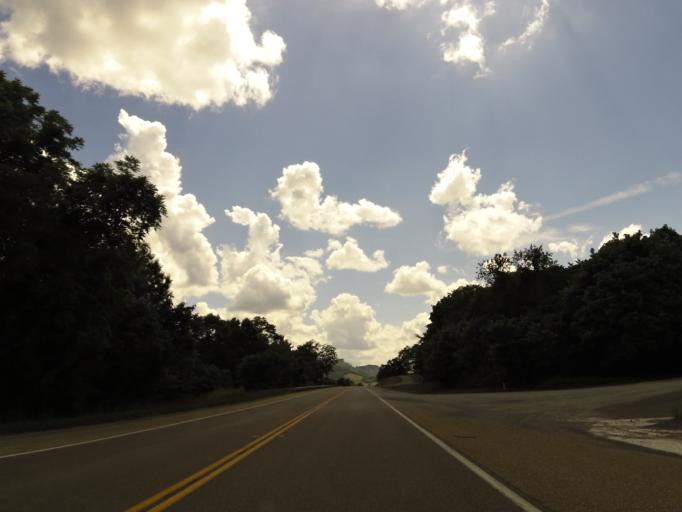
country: US
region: Virginia
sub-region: Lee County
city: Dryden
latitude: 36.7125
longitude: -82.9559
